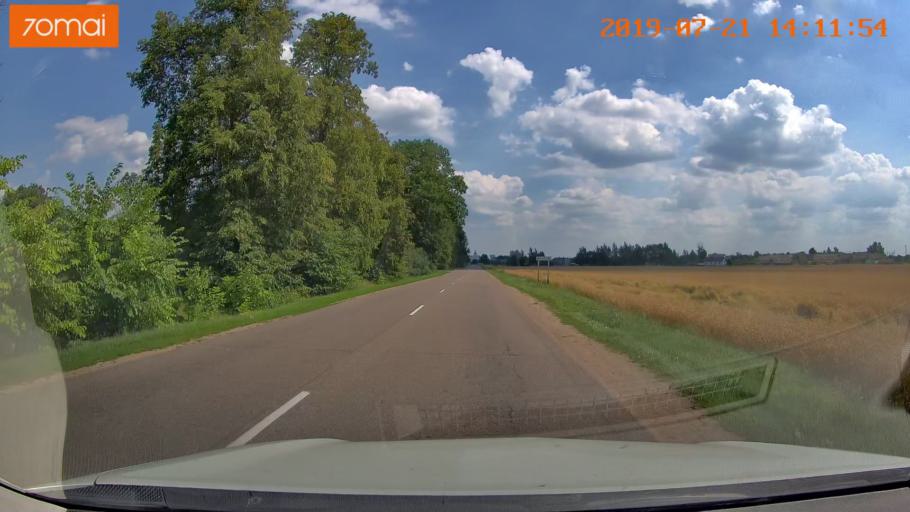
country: BY
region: Grodnenskaya
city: Karelichy
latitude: 53.6548
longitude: 26.1610
